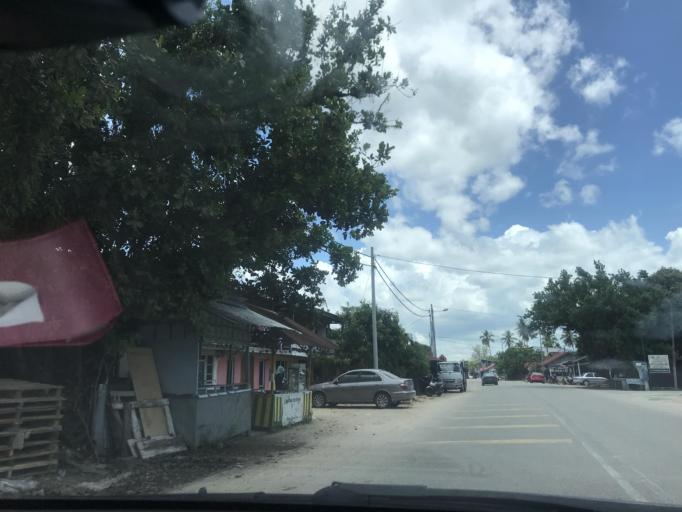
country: TH
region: Narathiwat
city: Tak Bai
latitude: 6.2294
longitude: 102.0975
